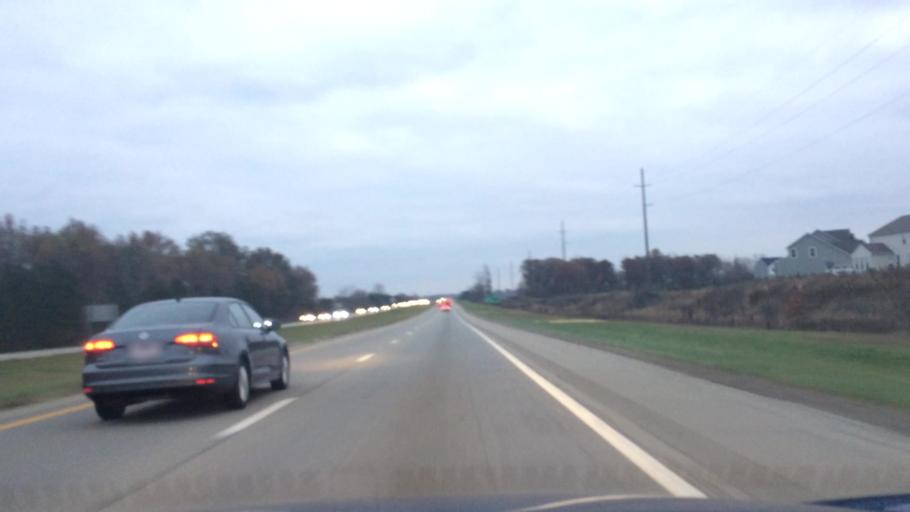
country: US
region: Ohio
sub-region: Union County
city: New California
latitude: 40.1528
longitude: -83.2213
